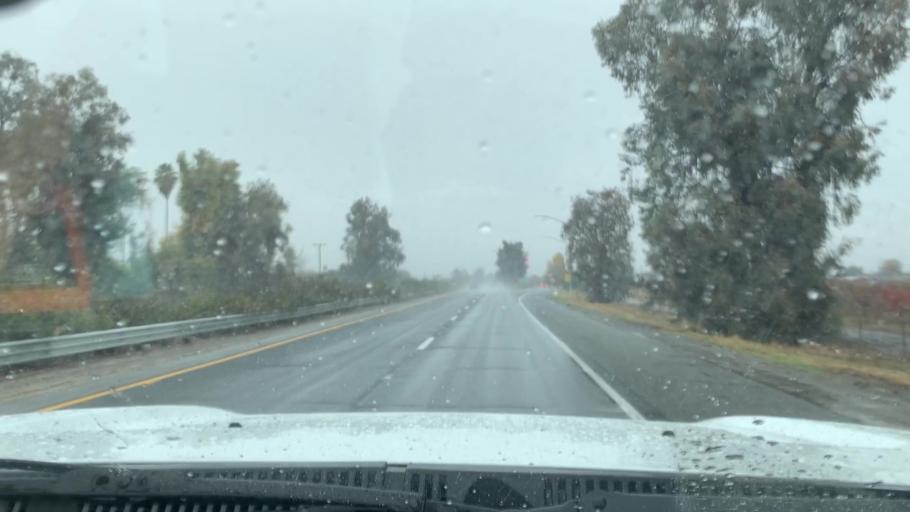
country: US
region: California
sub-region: Tulare County
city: Earlimart
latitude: 35.8732
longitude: -119.2705
